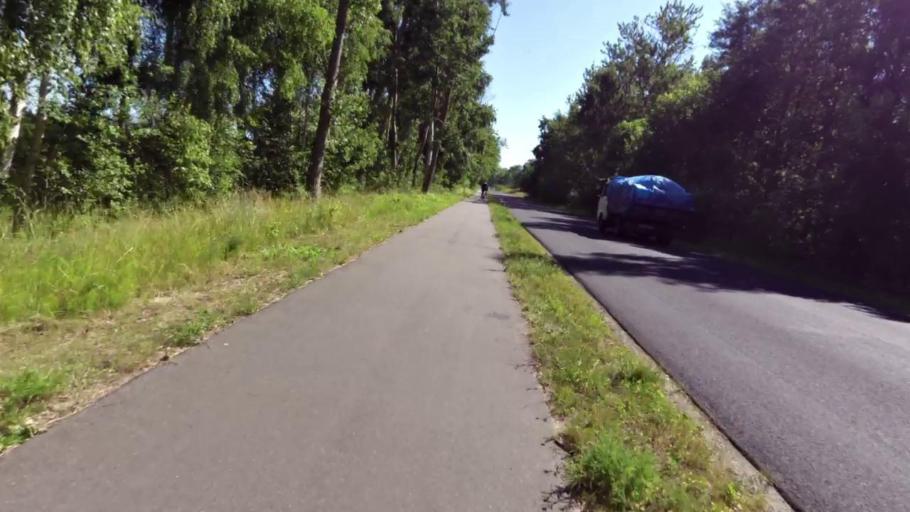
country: PL
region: West Pomeranian Voivodeship
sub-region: Powiat koszalinski
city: Mielno
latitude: 54.2868
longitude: 16.1483
